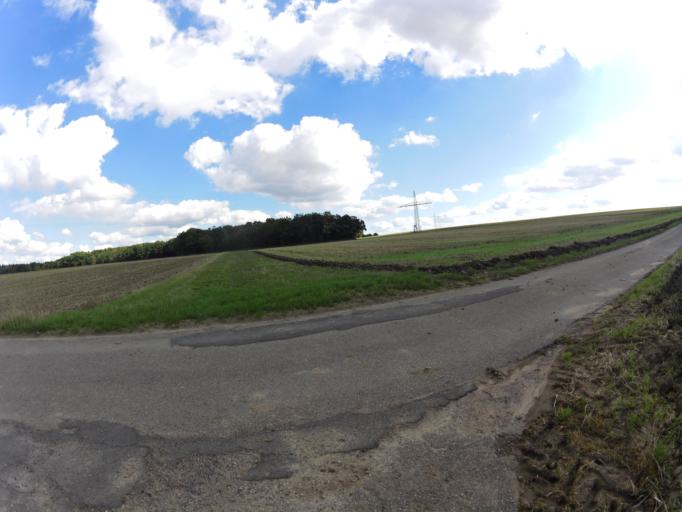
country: DE
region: Bavaria
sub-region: Regierungsbezirk Unterfranken
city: Frickenhausen
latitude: 49.6940
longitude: 10.0938
